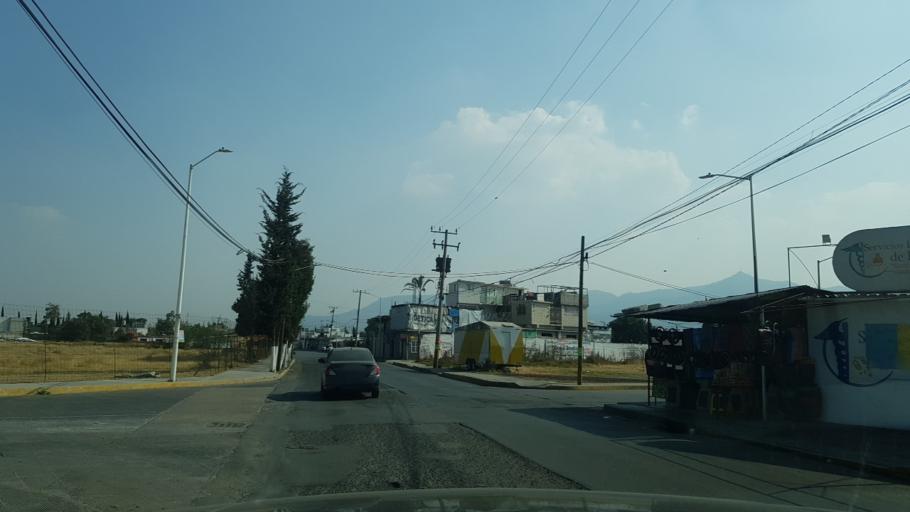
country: MX
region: Mexico
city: Santiago Teyahualco
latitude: 19.6595
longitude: -99.1274
